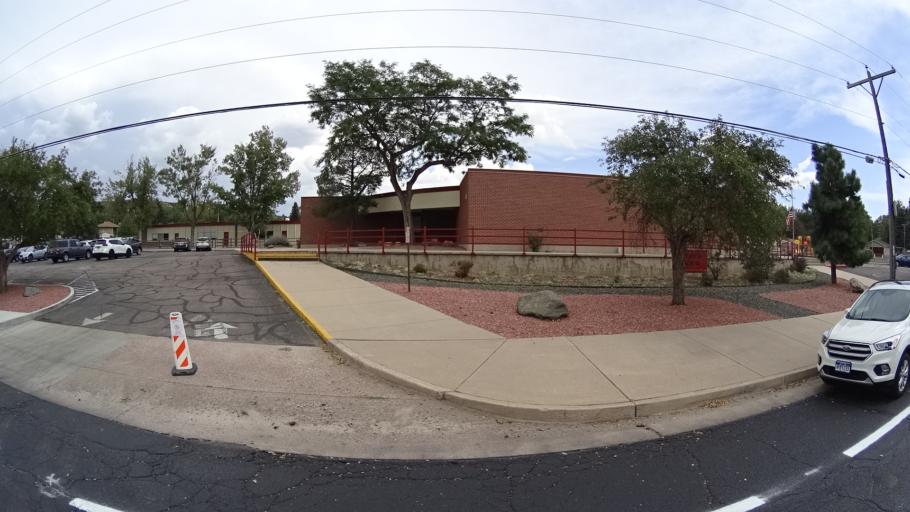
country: US
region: Colorado
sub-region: El Paso County
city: Colorado Springs
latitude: 38.8674
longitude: -104.7849
